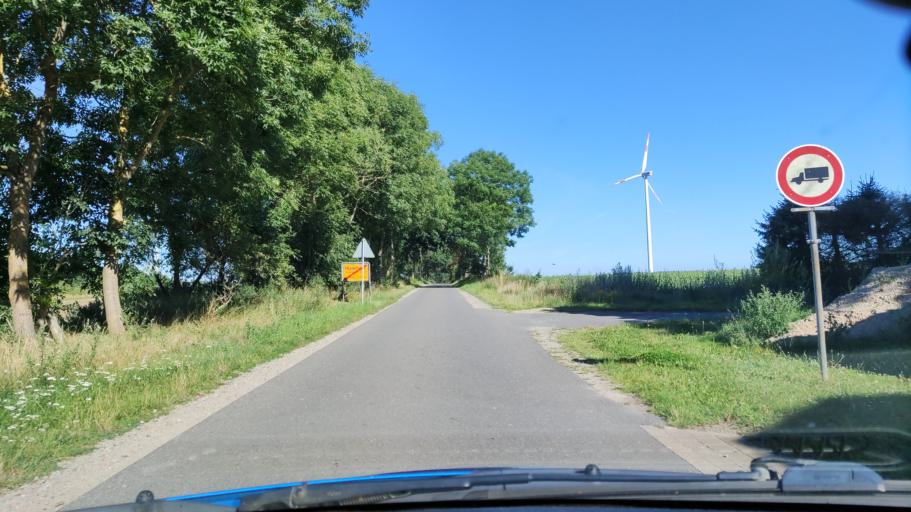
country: DE
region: Lower Saxony
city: Nahrendorf
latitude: 53.1803
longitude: 10.7846
